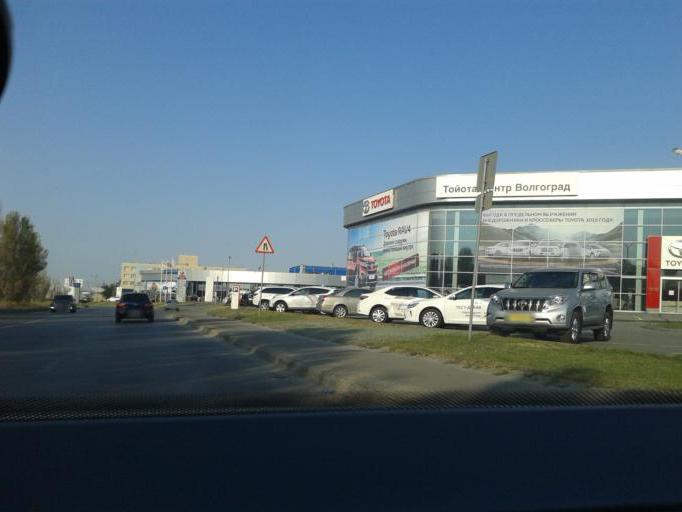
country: RU
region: Volgograd
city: Volgograd
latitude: 48.7538
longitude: 44.4797
